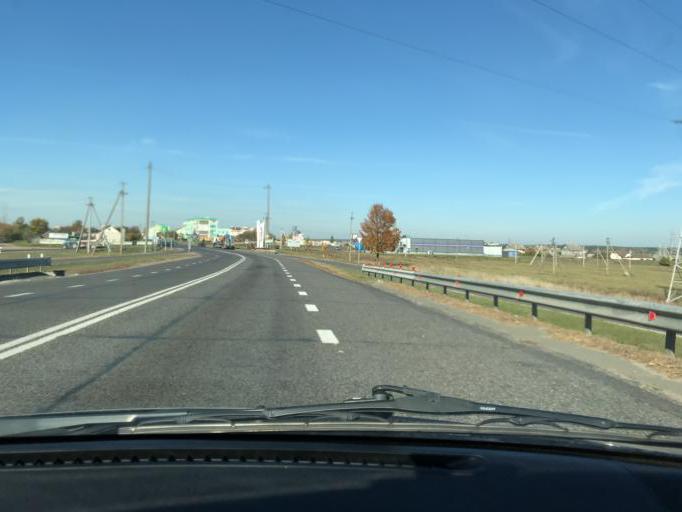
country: BY
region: Brest
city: Ivatsevichy
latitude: 52.7018
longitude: 25.3615
